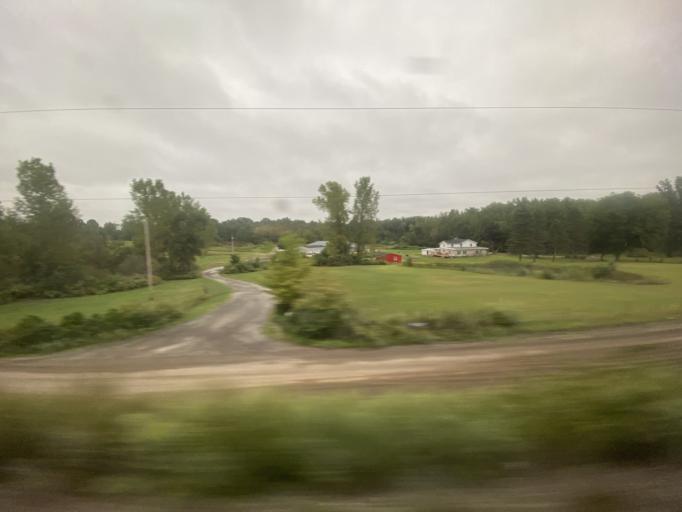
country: US
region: Indiana
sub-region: LaPorte County
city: Westville
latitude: 41.5990
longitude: -86.8881
